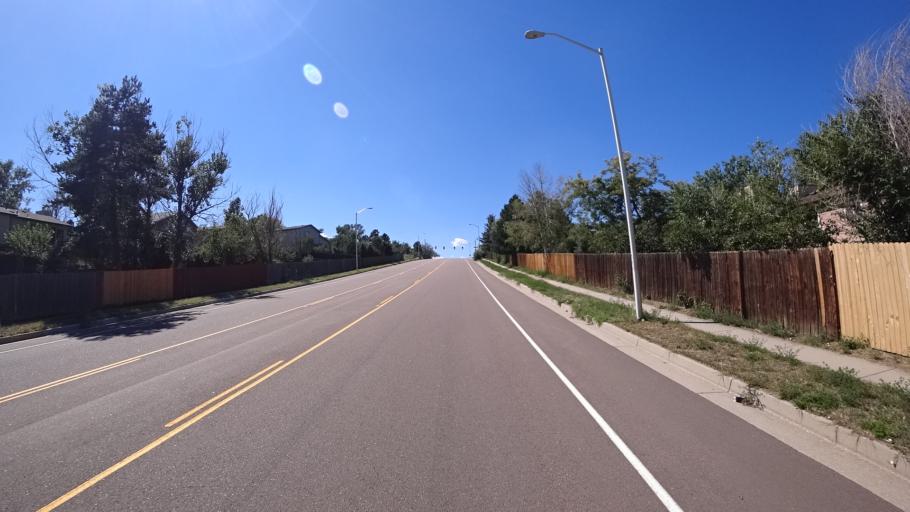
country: US
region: Colorado
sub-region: El Paso County
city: Cimarron Hills
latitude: 38.8769
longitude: -104.7261
